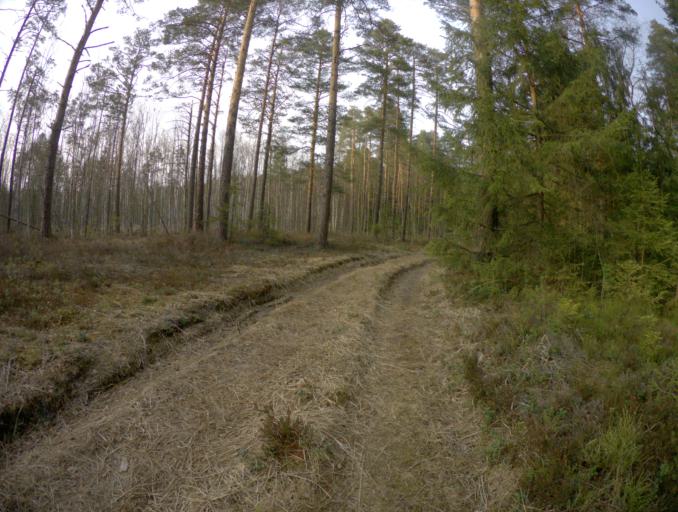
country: RU
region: Vladimir
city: Kommunar
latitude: 56.0760
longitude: 40.5205
